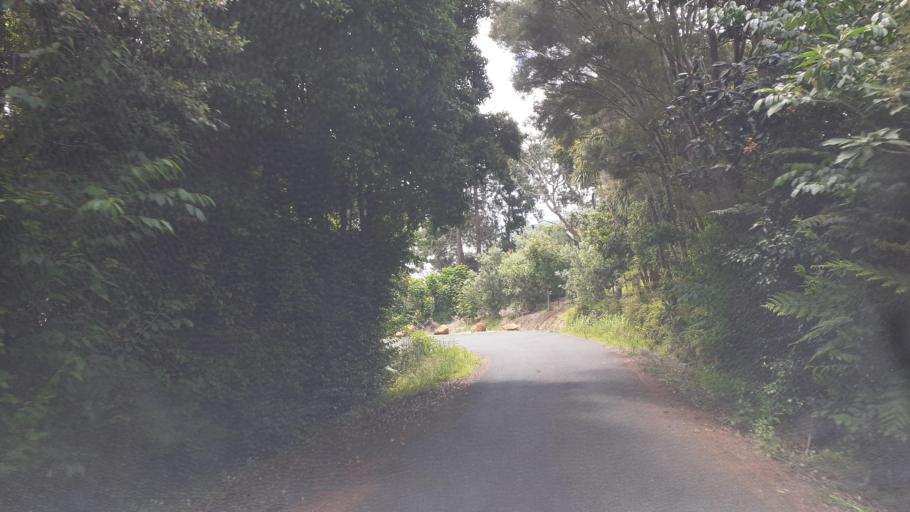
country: NZ
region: Northland
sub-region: Far North District
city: Paihia
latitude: -35.3081
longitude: 174.1121
